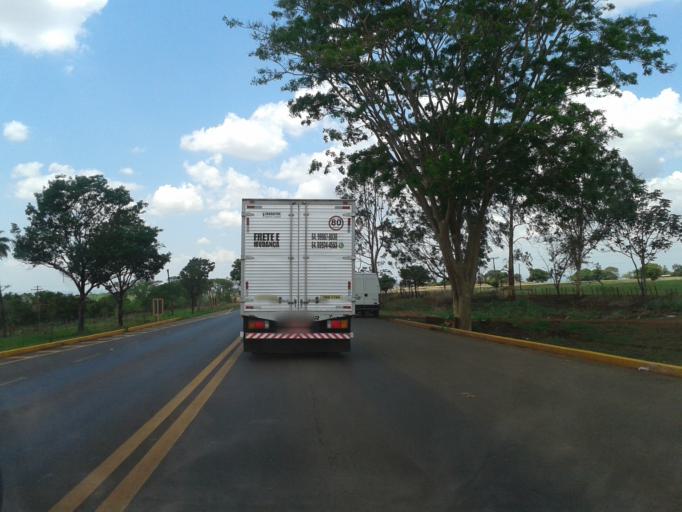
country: BR
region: Goias
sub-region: Itumbiara
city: Itumbiara
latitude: -18.3885
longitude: -49.3388
